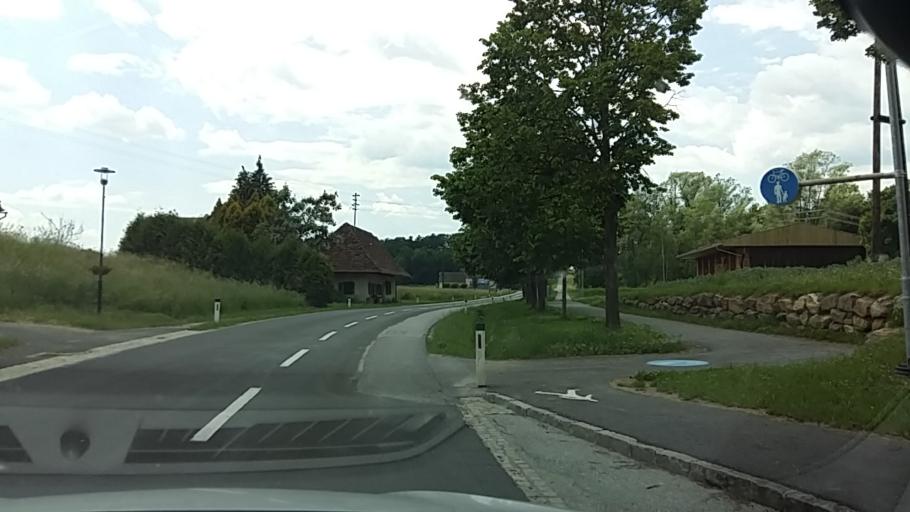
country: AT
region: Styria
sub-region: Politischer Bezirk Hartberg-Fuerstenfeld
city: Hainersdorf
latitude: 47.0934
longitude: 15.9557
